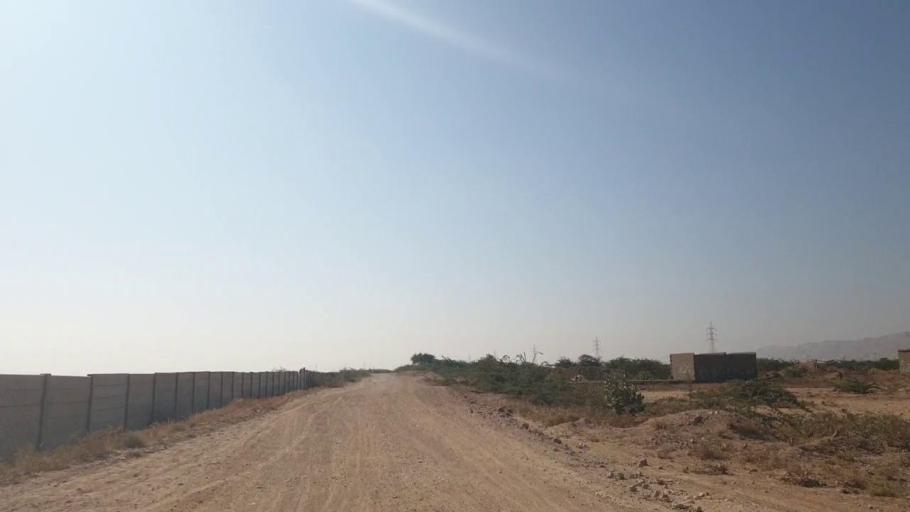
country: PK
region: Sindh
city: Gharo
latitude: 25.1569
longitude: 67.7270
